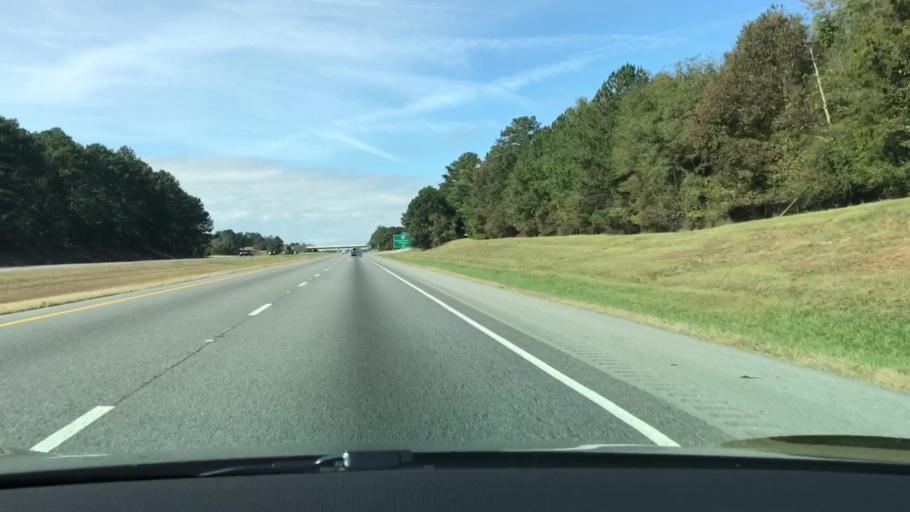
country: US
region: Georgia
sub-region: Walton County
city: Social Circle
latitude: 33.6082
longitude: -83.6906
